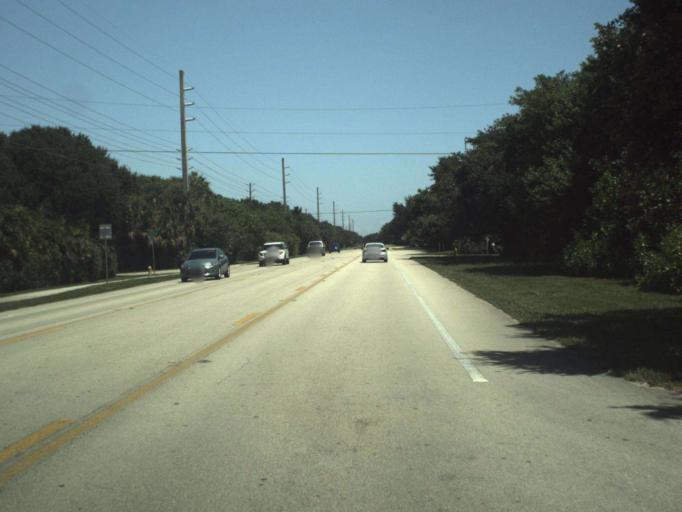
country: US
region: Florida
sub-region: Indian River County
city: Indian River Shores
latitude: 27.6802
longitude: -80.3663
